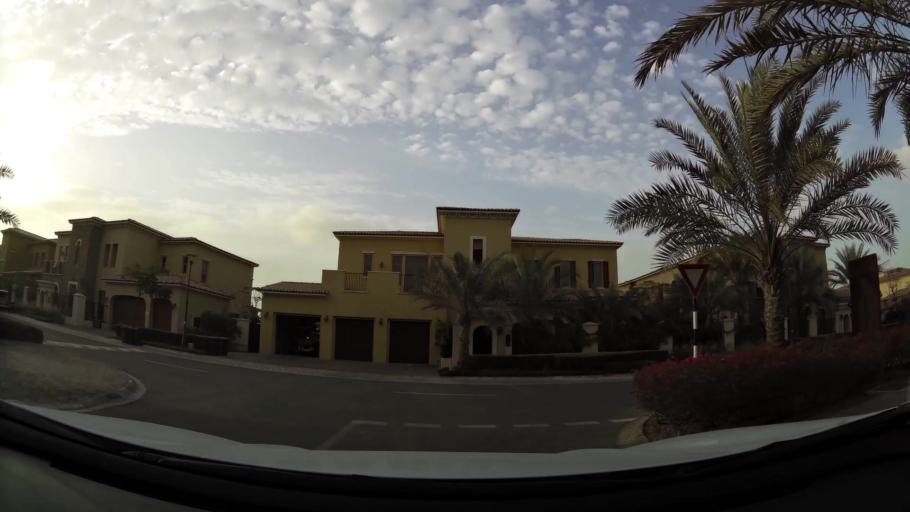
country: AE
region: Abu Dhabi
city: Abu Dhabi
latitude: 24.5358
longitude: 54.4323
